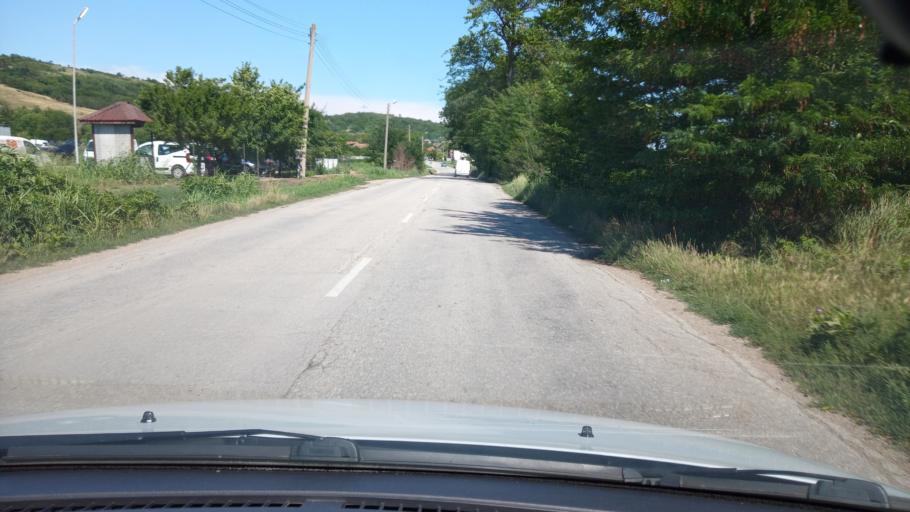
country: BG
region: Pleven
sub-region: Obshtina Dolna Mitropoliya
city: Dolna Mitropoliya
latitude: 43.4488
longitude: 24.5663
